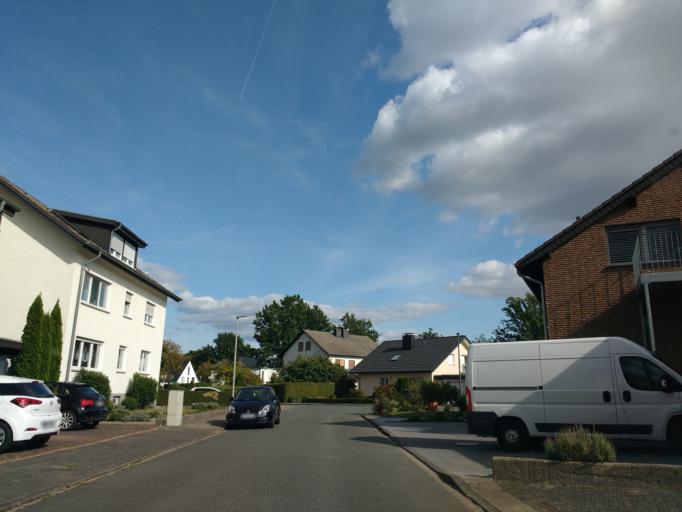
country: DE
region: North Rhine-Westphalia
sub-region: Regierungsbezirk Detmold
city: Hovelhof
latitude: 51.7452
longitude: 8.6805
